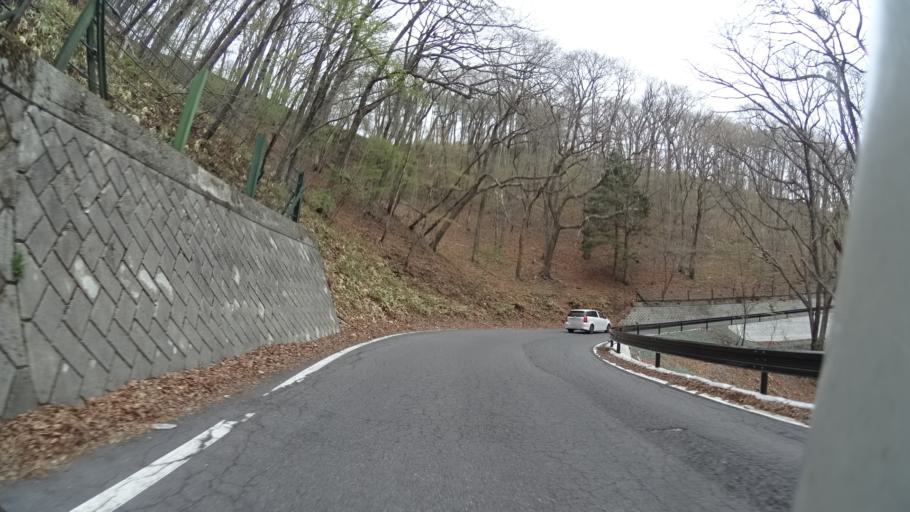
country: JP
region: Nagano
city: Suwa
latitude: 36.1372
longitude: 138.1378
